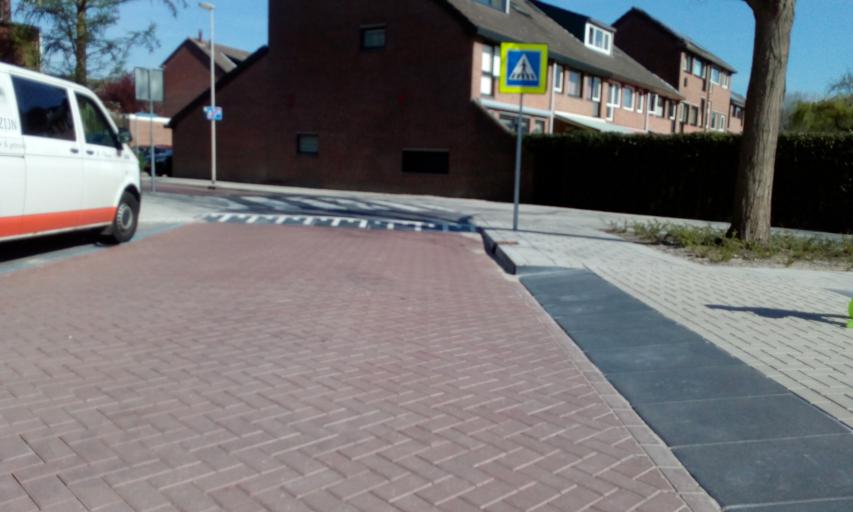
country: NL
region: South Holland
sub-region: Gemeente Zoetermeer
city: Zoetermeer
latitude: 52.0656
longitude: 4.4852
